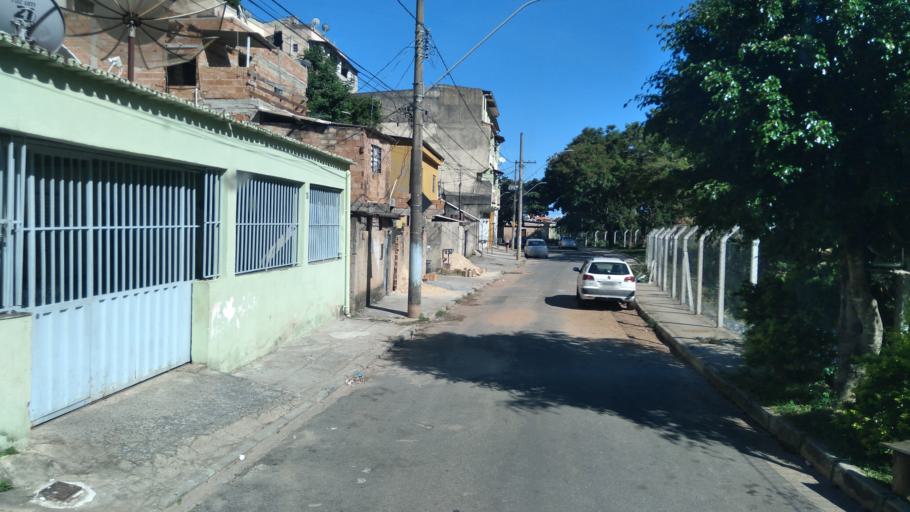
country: BR
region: Minas Gerais
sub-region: Belo Horizonte
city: Belo Horizonte
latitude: -19.9188
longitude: -43.8905
